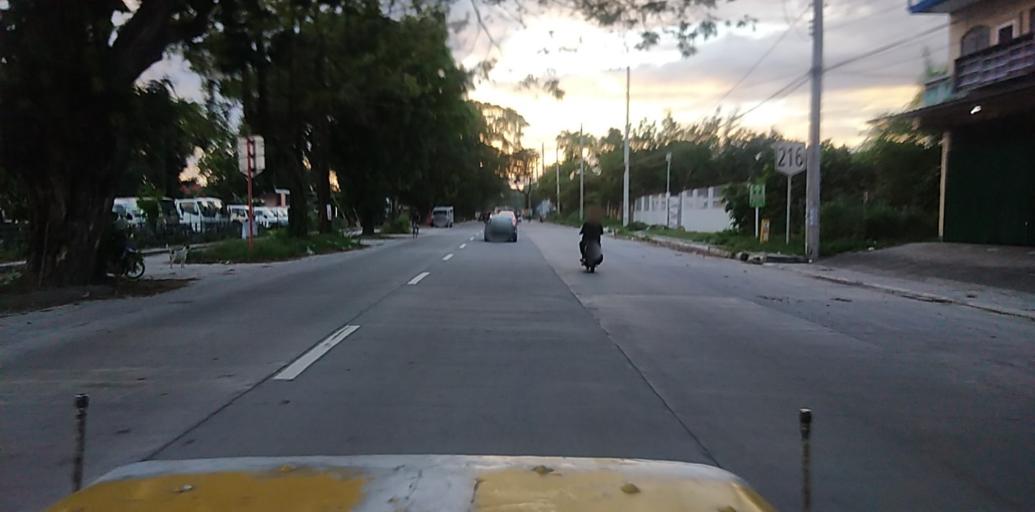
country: PH
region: Central Luzon
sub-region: Province of Pampanga
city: Calibutbut
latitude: 15.1168
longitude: 120.6011
